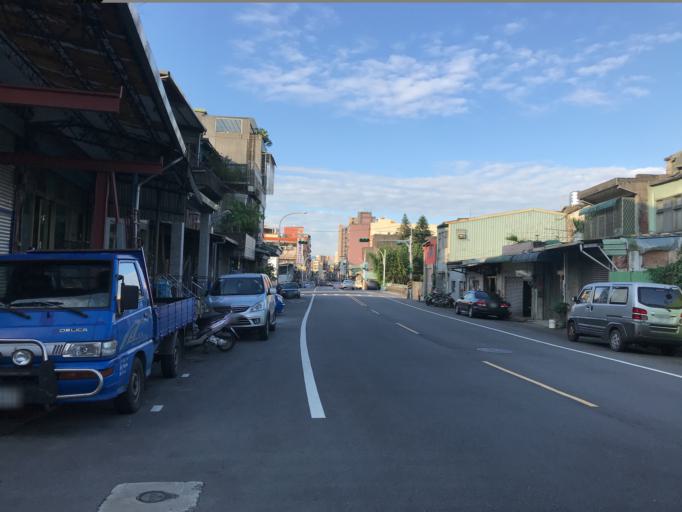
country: TW
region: Taiwan
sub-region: Taoyuan
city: Taoyuan
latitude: 24.9233
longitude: 121.3673
